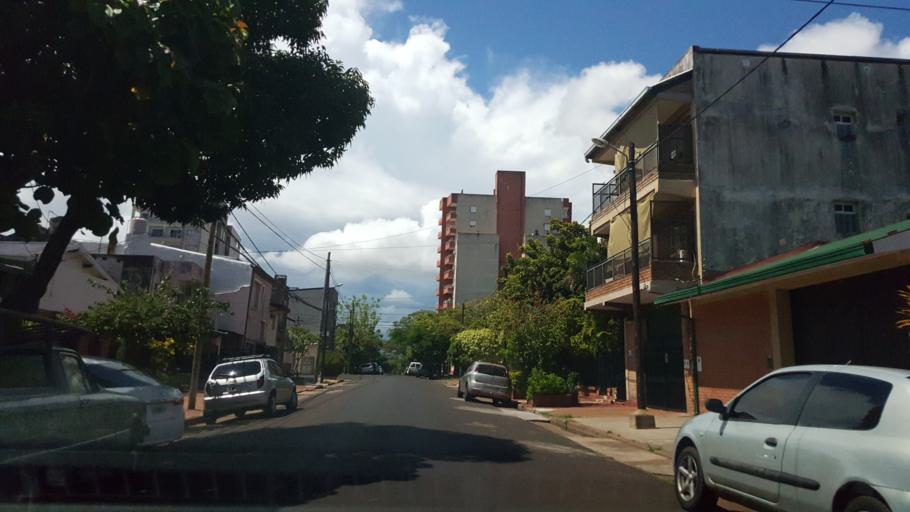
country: AR
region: Misiones
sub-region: Departamento de Capital
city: Posadas
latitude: -27.3575
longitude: -55.8976
